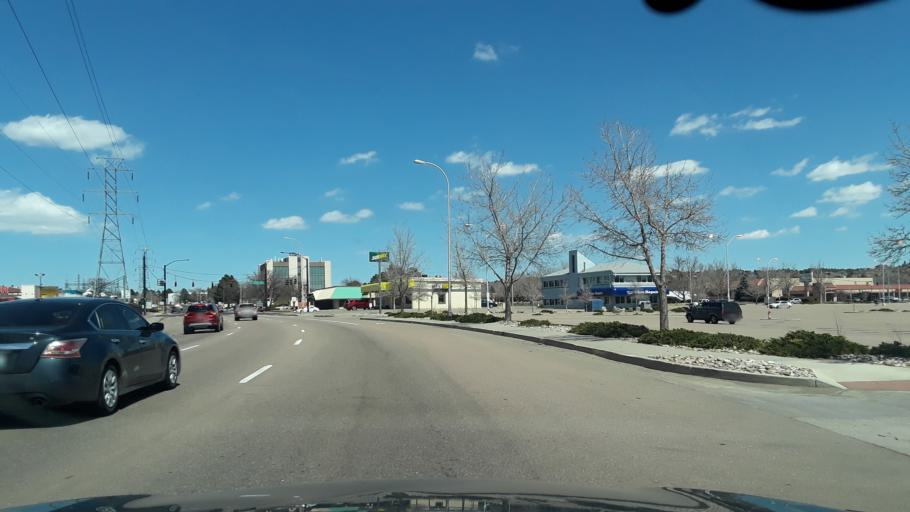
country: US
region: Colorado
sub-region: El Paso County
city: Cimarron Hills
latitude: 38.8530
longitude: -104.7566
